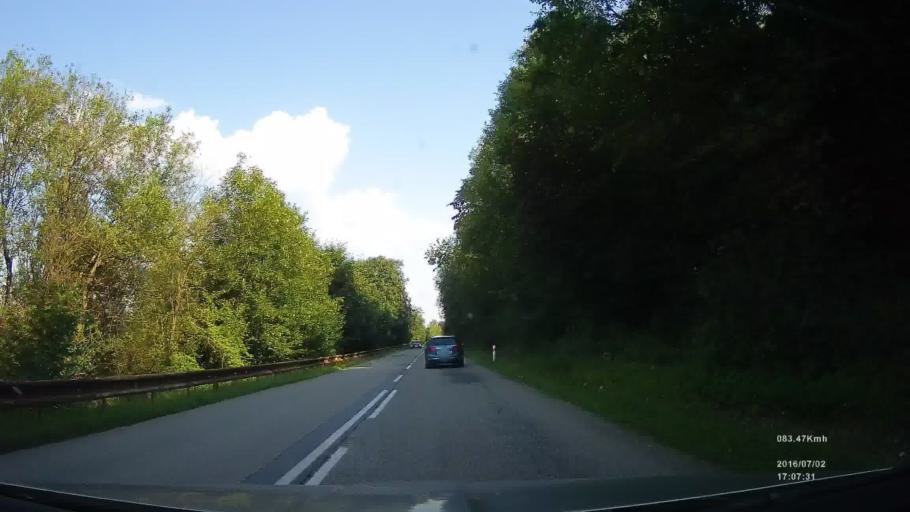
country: SK
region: Kosicky
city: Gelnica
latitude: 48.8475
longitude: 21.0333
